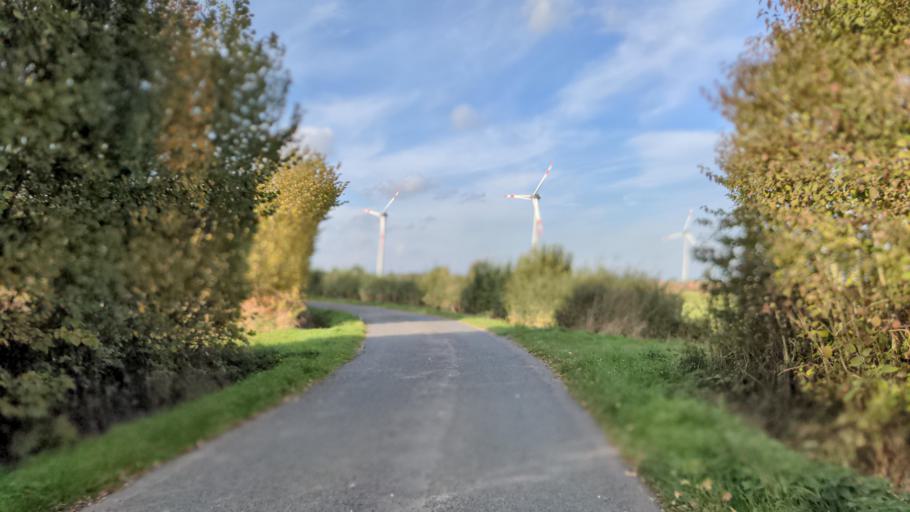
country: DE
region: Schleswig-Holstein
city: Monkhagen
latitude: 53.9298
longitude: 10.5747
